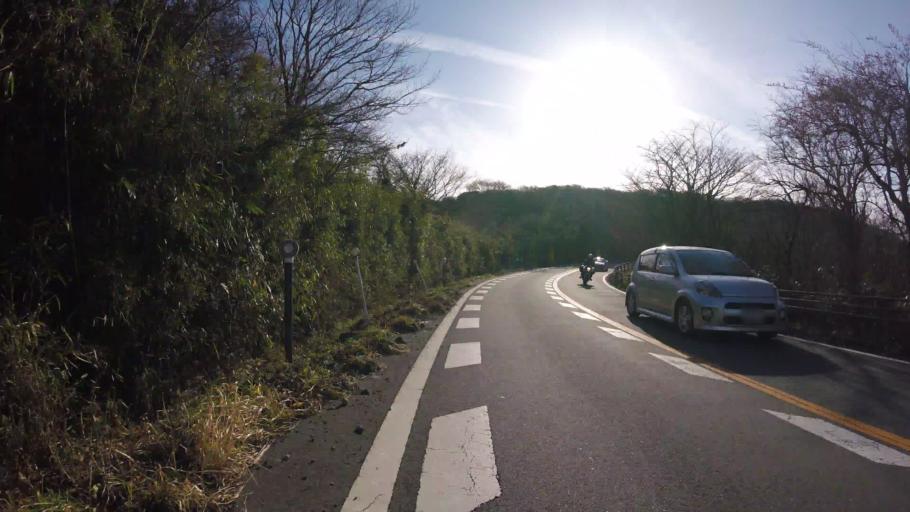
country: JP
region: Kanagawa
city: Hakone
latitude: 35.1627
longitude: 139.0277
